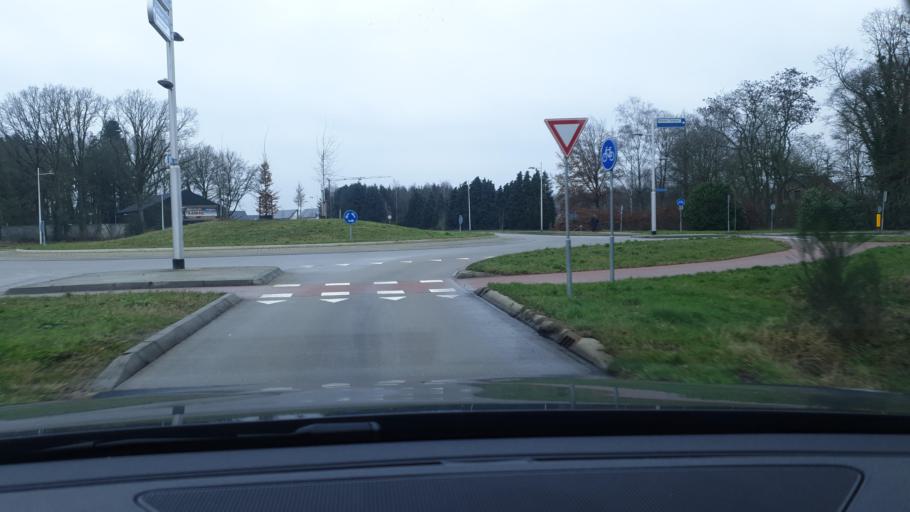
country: NL
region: North Brabant
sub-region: Gemeente Veldhoven
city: Oerle
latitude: 51.4030
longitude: 5.3766
